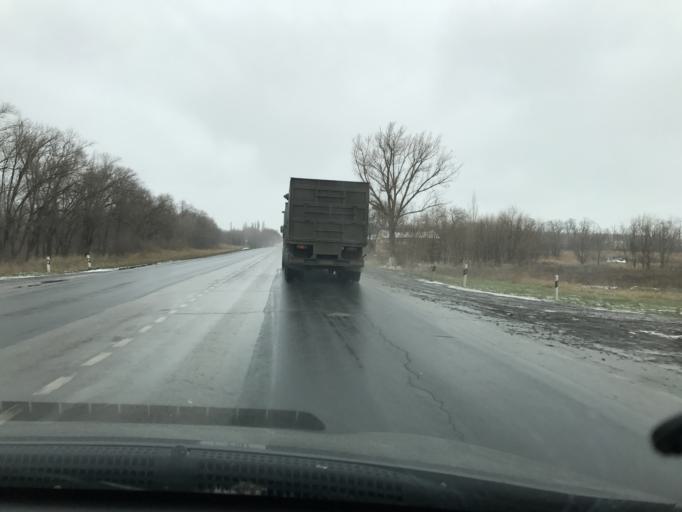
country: RU
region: Rostov
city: Zernograd
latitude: 46.8349
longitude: 40.2321
